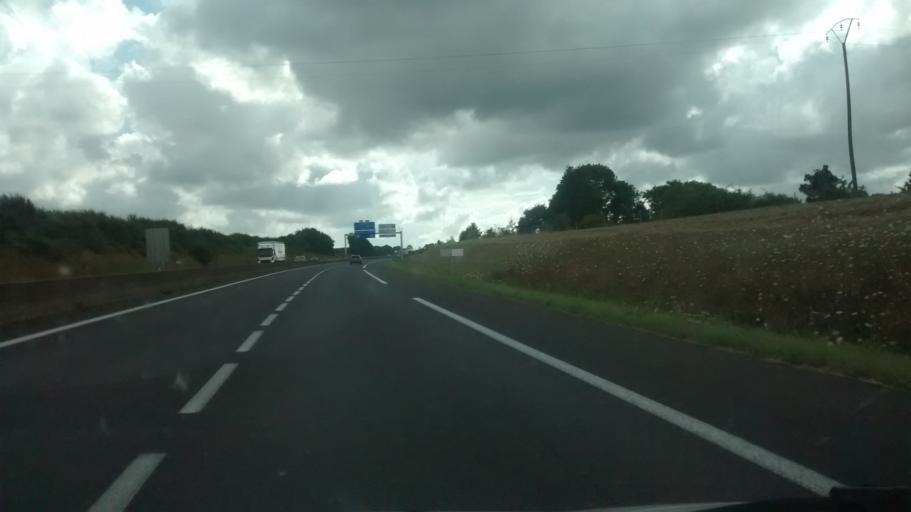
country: FR
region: Lower Normandy
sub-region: Departement du Calvados
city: Villers-Bocage
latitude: 49.0535
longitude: -0.7043
